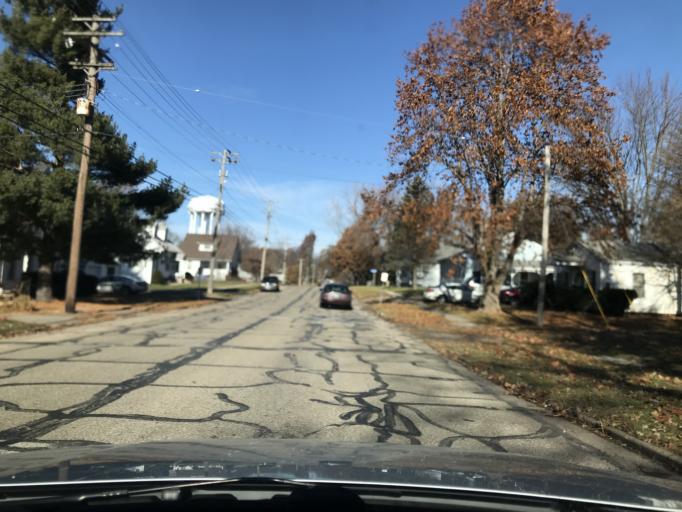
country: US
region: Illinois
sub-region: McDonough County
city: Macomb
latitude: 40.4501
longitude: -90.6673
